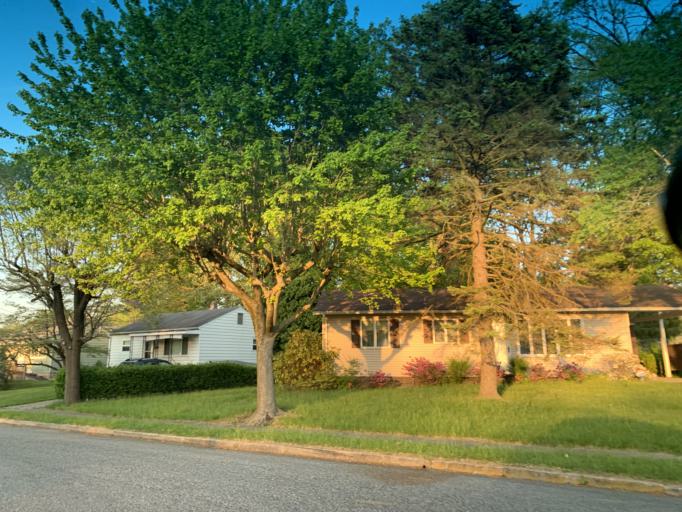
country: US
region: Maryland
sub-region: Harford County
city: Aberdeen
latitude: 39.5018
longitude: -76.1741
